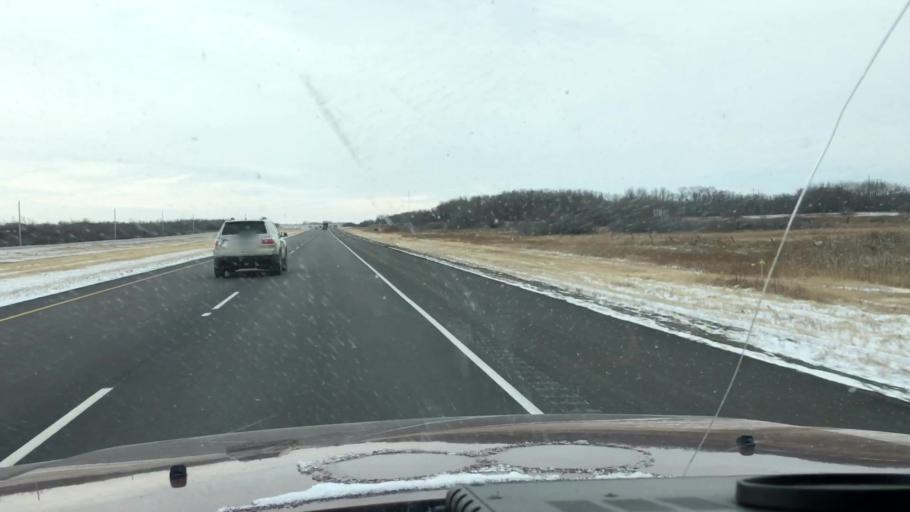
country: CA
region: Saskatchewan
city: Saskatoon
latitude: 51.8814
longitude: -106.5128
